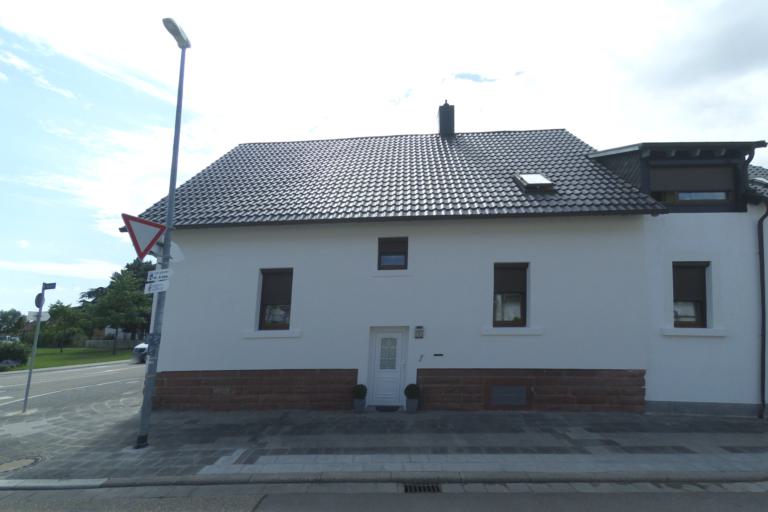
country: DE
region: Rheinland-Pfalz
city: Schifferstadt
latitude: 49.3855
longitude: 8.3647
